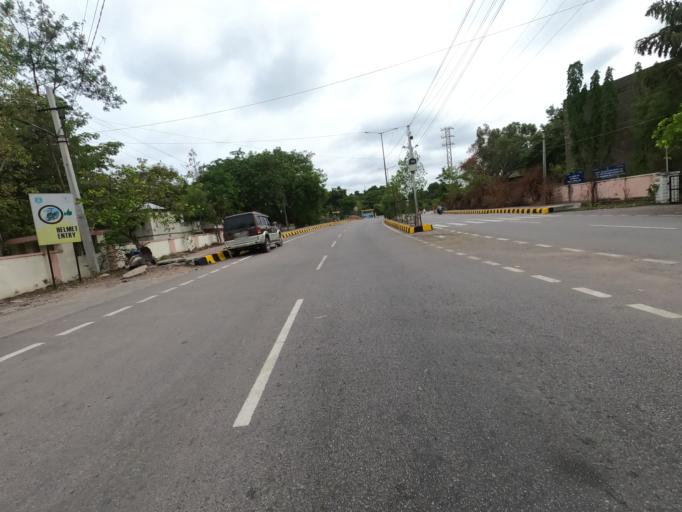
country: IN
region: Telangana
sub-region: Hyderabad
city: Hyderabad
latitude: 17.3344
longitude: 78.4098
